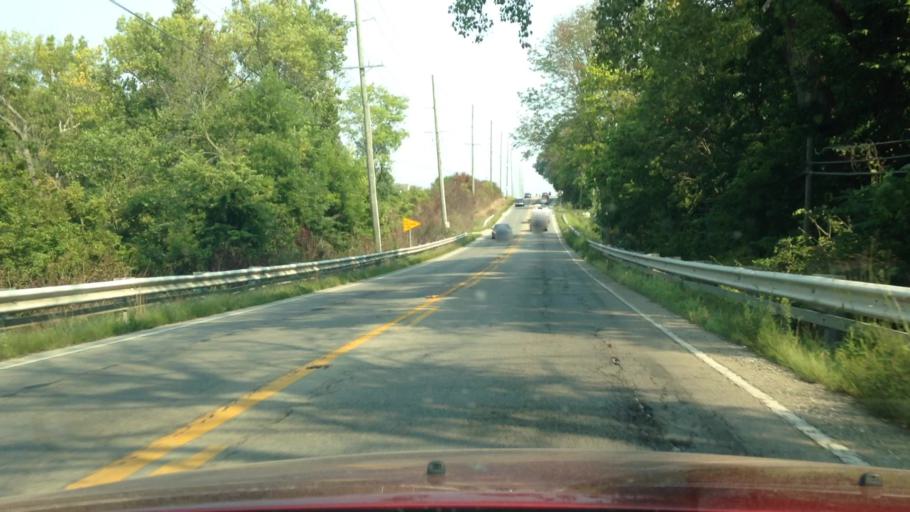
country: US
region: Indiana
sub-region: Johnson County
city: Waterloo
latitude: 39.5669
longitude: -86.1588
